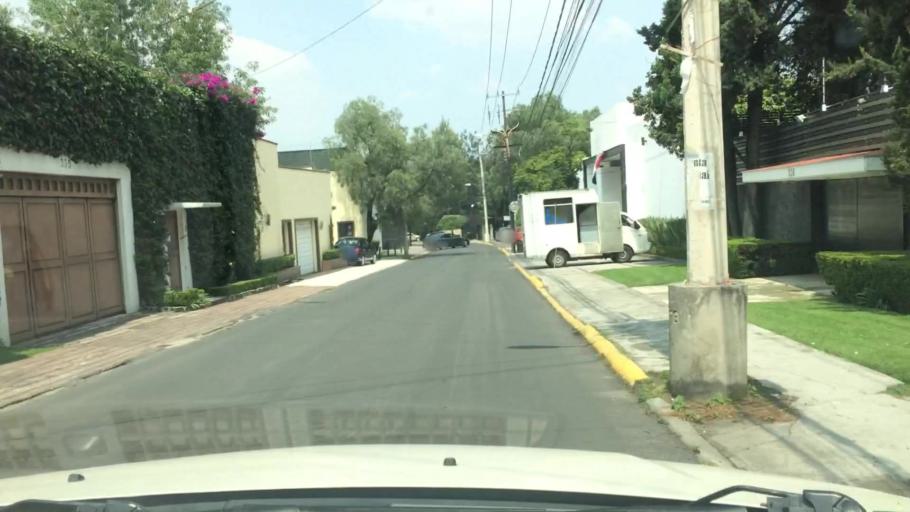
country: MX
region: Mexico City
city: Magdalena Contreras
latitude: 19.3221
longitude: -99.2086
